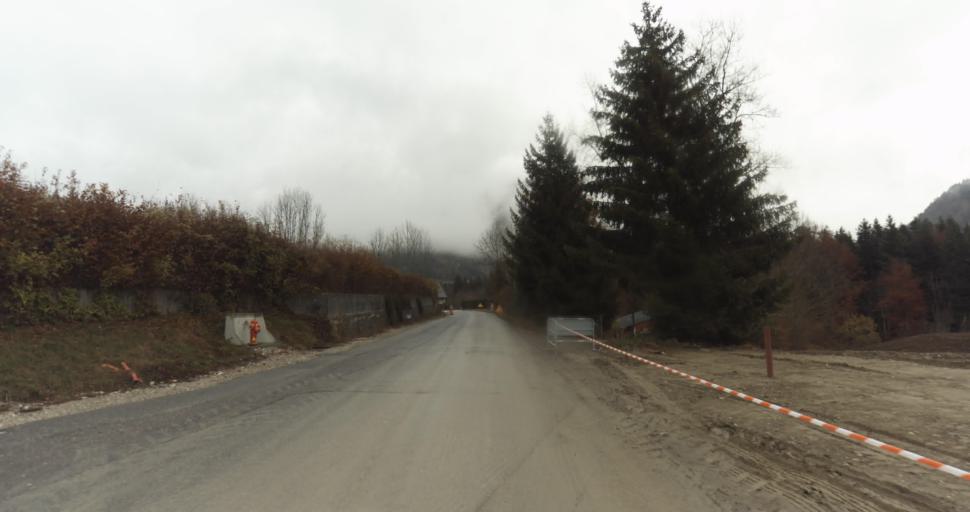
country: FR
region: Rhone-Alpes
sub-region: Departement de la Haute-Savoie
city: Thorens-Glieres
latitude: 45.9939
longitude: 6.2498
